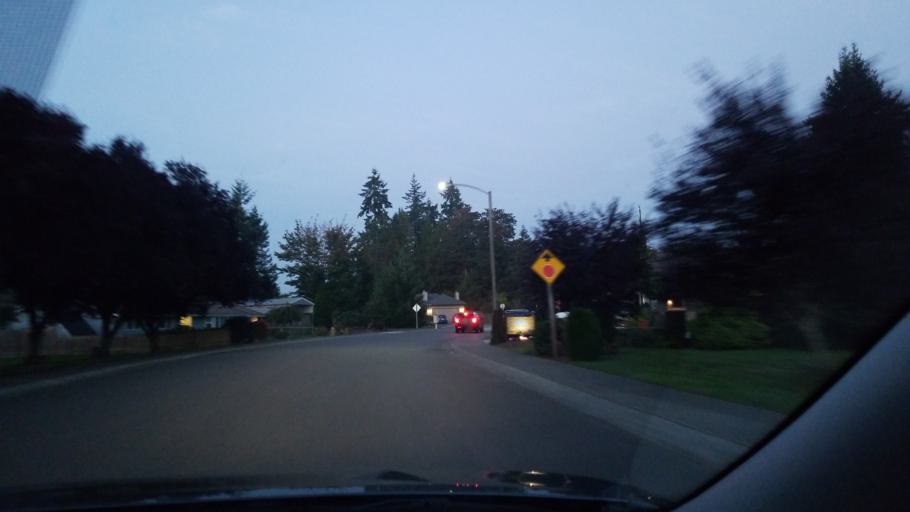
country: US
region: Washington
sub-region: Snohomish County
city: Silver Firs
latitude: 47.8807
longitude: -122.1731
